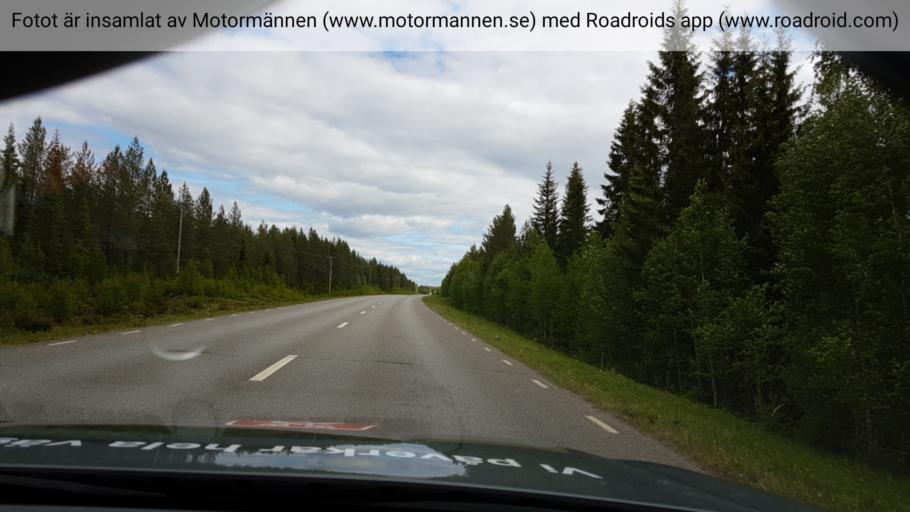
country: SE
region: Jaemtland
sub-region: Stroemsunds Kommun
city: Stroemsund
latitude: 64.2923
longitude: 15.3395
